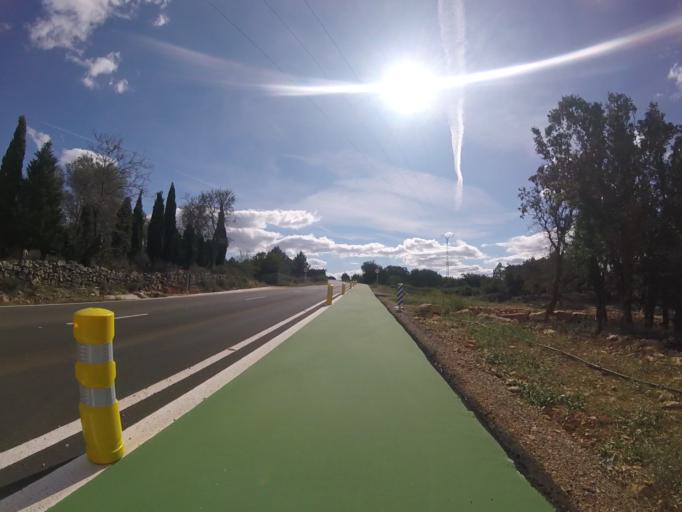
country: ES
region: Valencia
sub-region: Provincia de Castello
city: Albocasser
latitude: 40.4124
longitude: 0.0711
